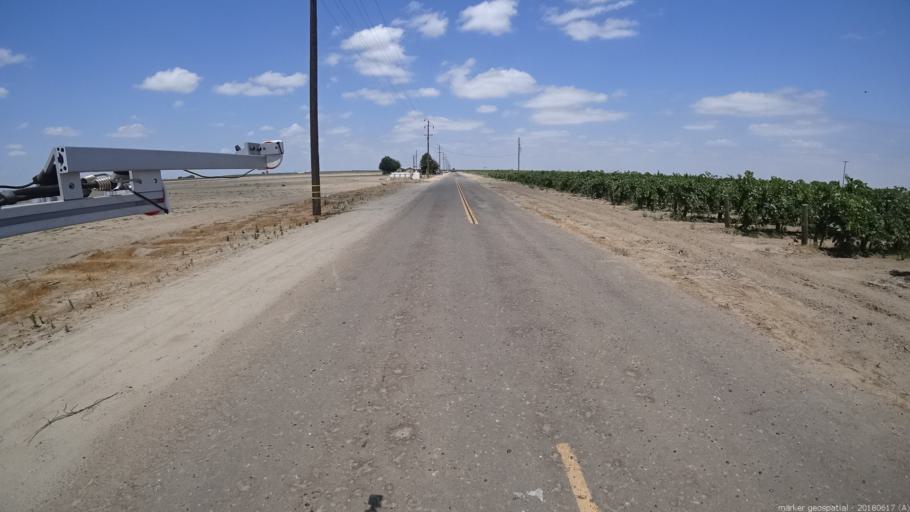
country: US
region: California
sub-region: Fresno County
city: Biola
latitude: 36.8286
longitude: -120.1150
